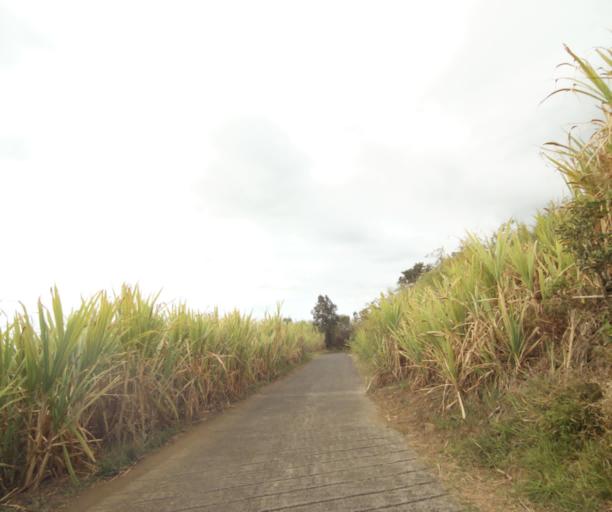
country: RE
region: Reunion
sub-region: Reunion
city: Saint-Paul
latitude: -21.0241
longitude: 55.3223
